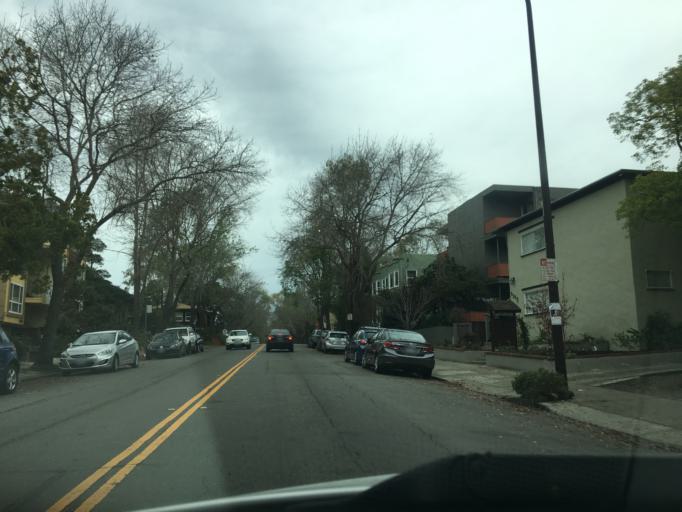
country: US
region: California
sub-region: Alameda County
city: Berkeley
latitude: 37.8823
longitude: -122.2742
